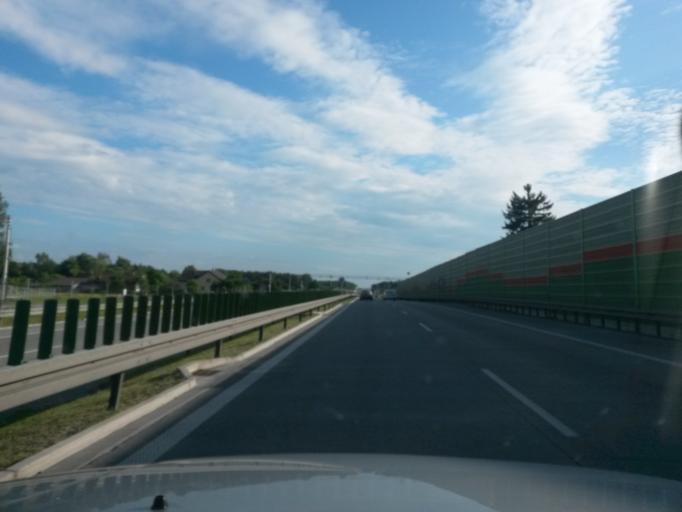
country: PL
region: Lodz Voivodeship
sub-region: Powiat rawski
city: Rawa Mazowiecka
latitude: 51.7429
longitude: 20.2359
